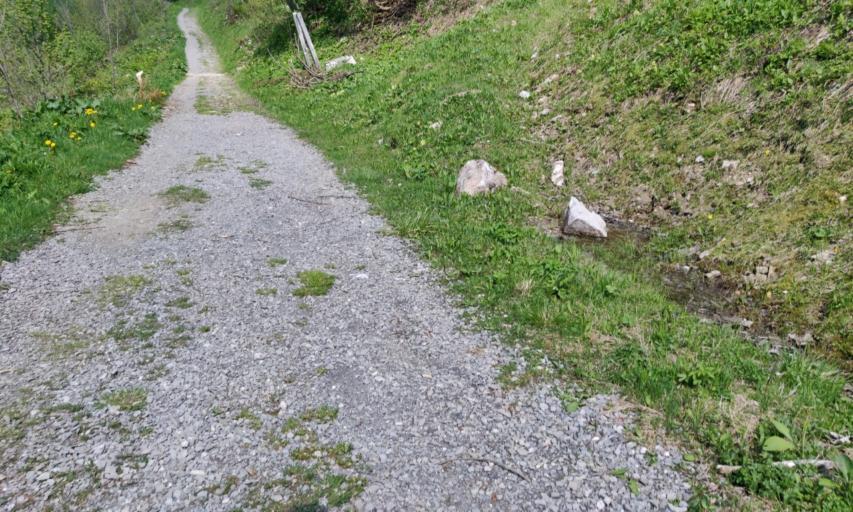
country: CH
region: Fribourg
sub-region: Gruyere District
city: Vuadens
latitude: 46.5449
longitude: 6.9978
